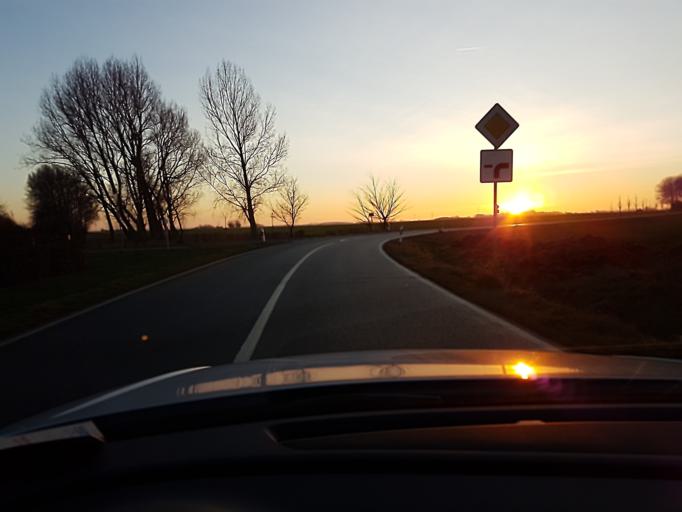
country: DE
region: Mecklenburg-Vorpommern
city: Wiek
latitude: 54.5853
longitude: 13.2848
